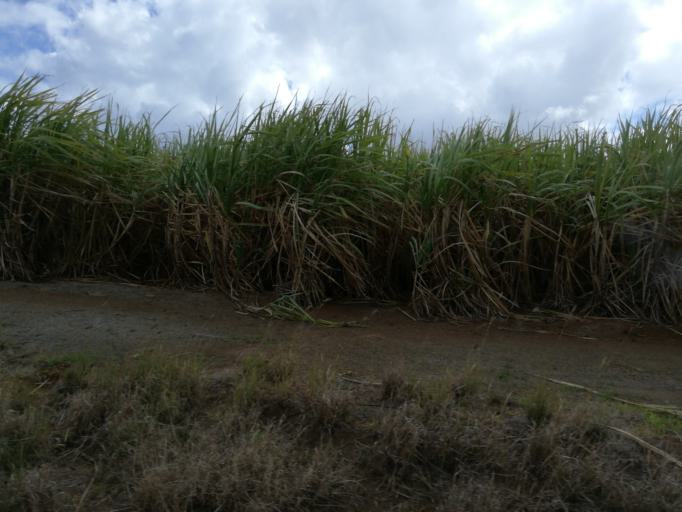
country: MU
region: Pamplemousses
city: Arsenal
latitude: -20.1026
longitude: 57.5448
